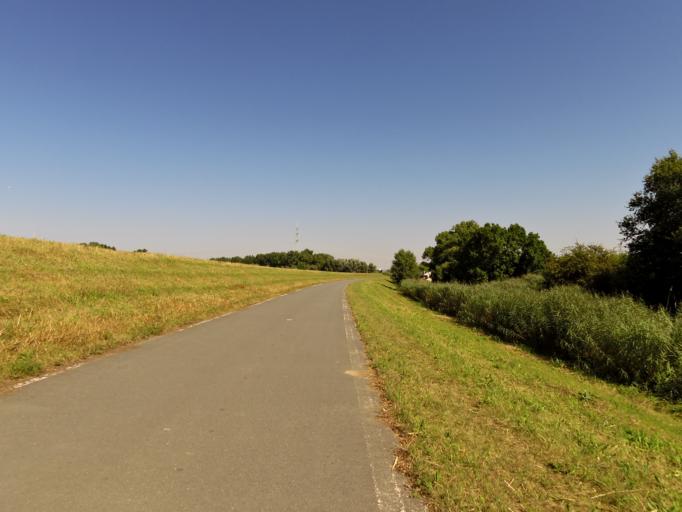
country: DE
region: Hesse
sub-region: Regierungsbezirk Darmstadt
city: Ginsheim-Gustavsburg
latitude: 49.9536
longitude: 8.3575
